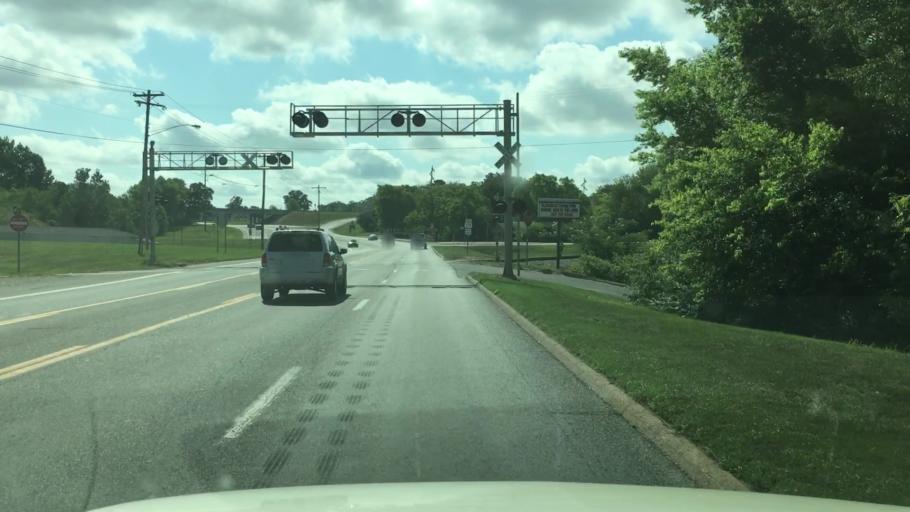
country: US
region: Arkansas
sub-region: Garland County
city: Piney
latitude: 34.4935
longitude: -93.1164
